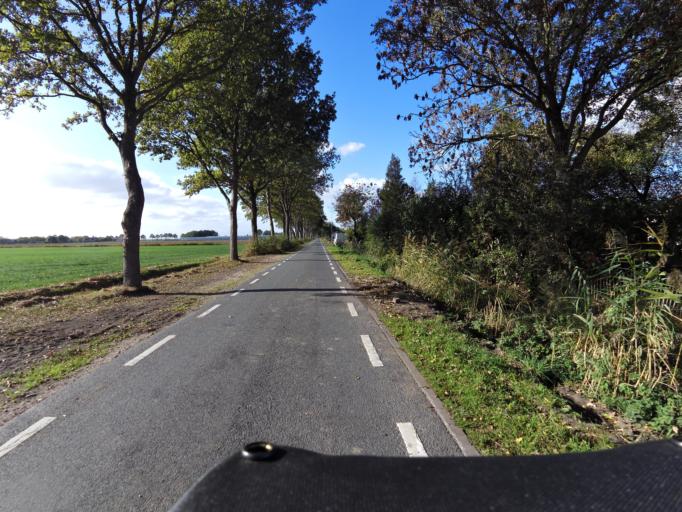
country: NL
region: North Brabant
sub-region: Gemeente Bergen op Zoom
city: Lepelstraat
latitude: 51.5569
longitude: 4.2741
